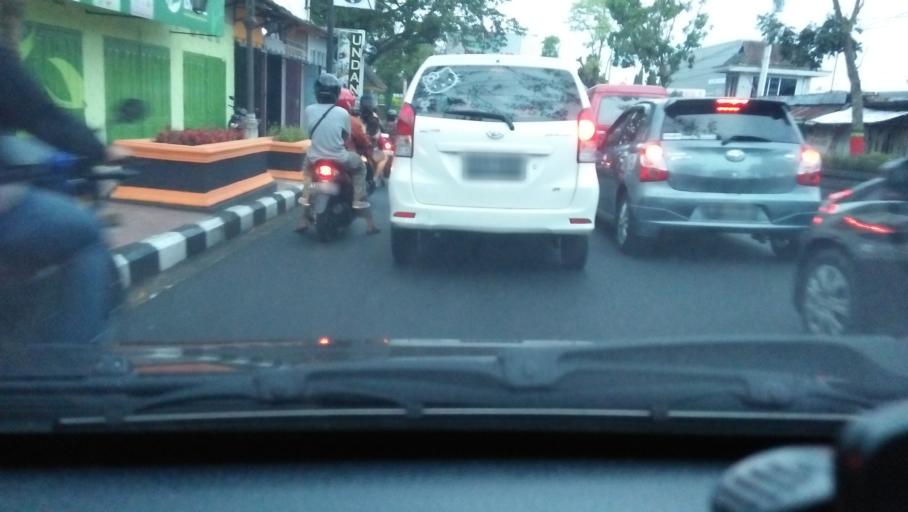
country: ID
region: Central Java
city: Mertoyudan
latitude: -7.5010
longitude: 110.2236
